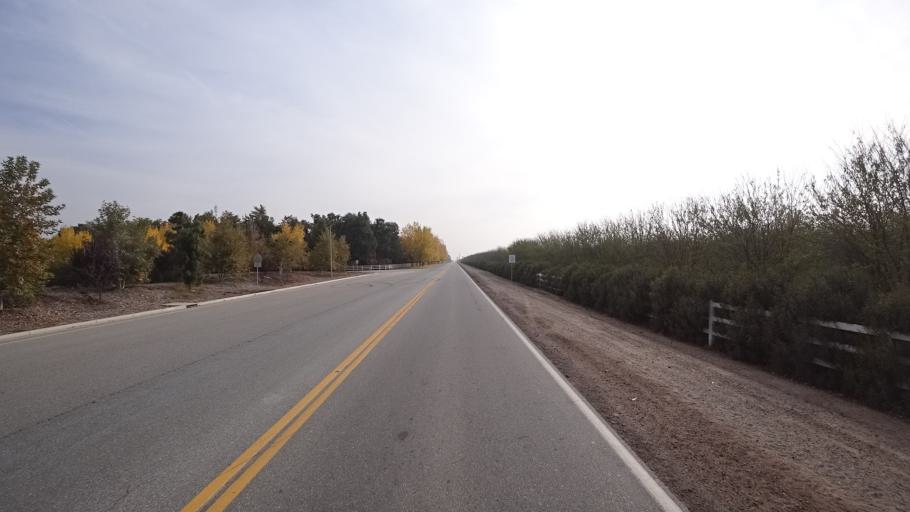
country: US
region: California
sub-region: Kern County
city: Greenacres
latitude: 35.2933
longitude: -119.1282
